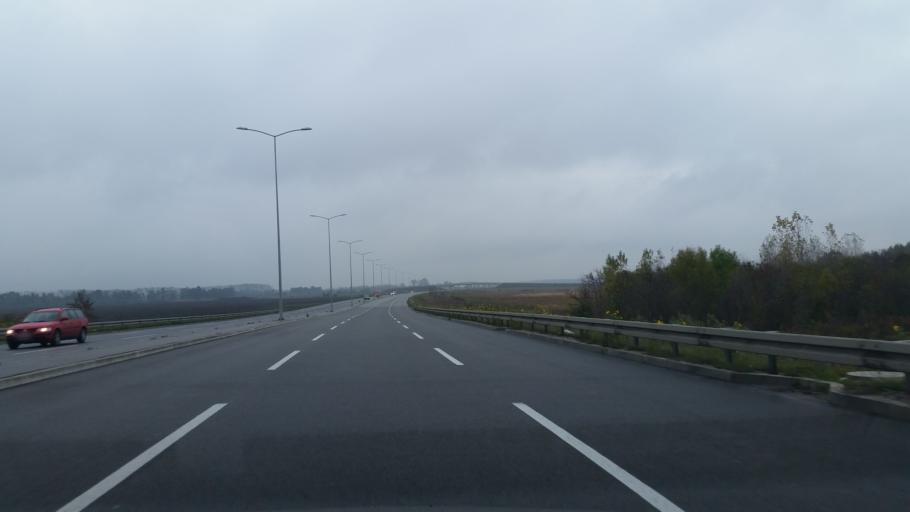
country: RS
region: Central Serbia
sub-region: Belgrade
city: Zemun
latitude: 44.8897
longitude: 20.4059
